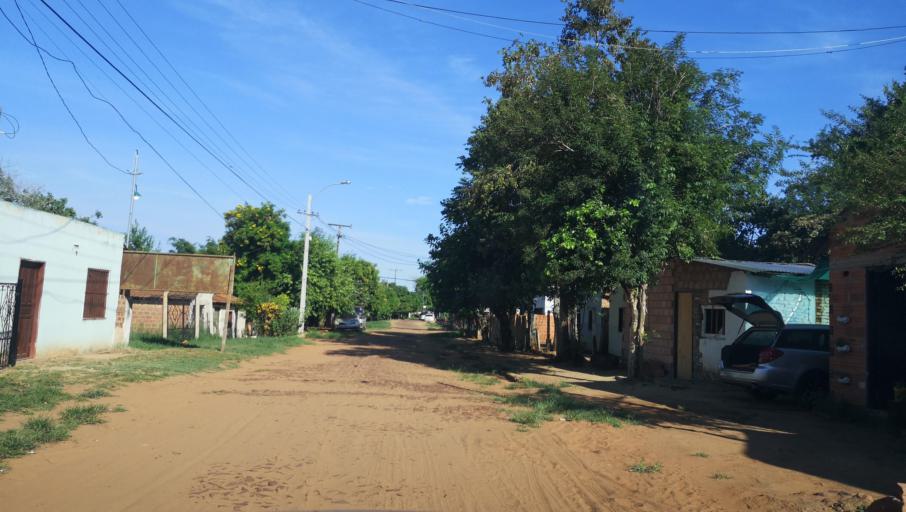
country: PY
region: Misiones
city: Santa Maria
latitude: -26.8834
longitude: -57.0099
